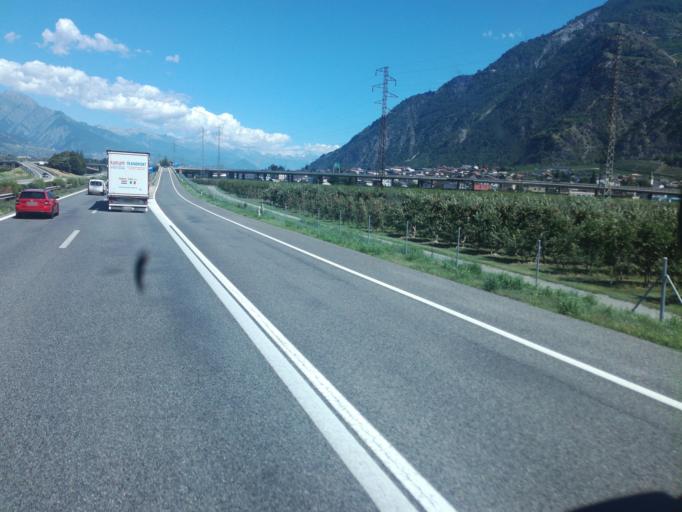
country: CH
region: Valais
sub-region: Martigny District
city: Riddes
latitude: 46.1693
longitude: 7.2092
